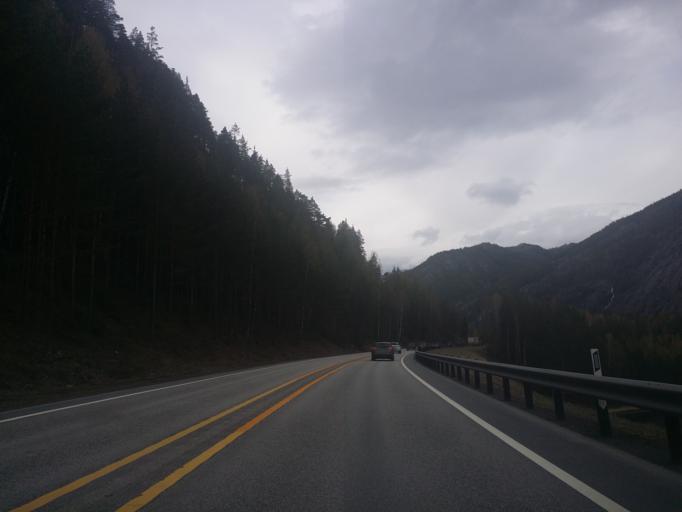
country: NO
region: Buskerud
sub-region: Fla
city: Fla
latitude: 60.4408
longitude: 9.3135
